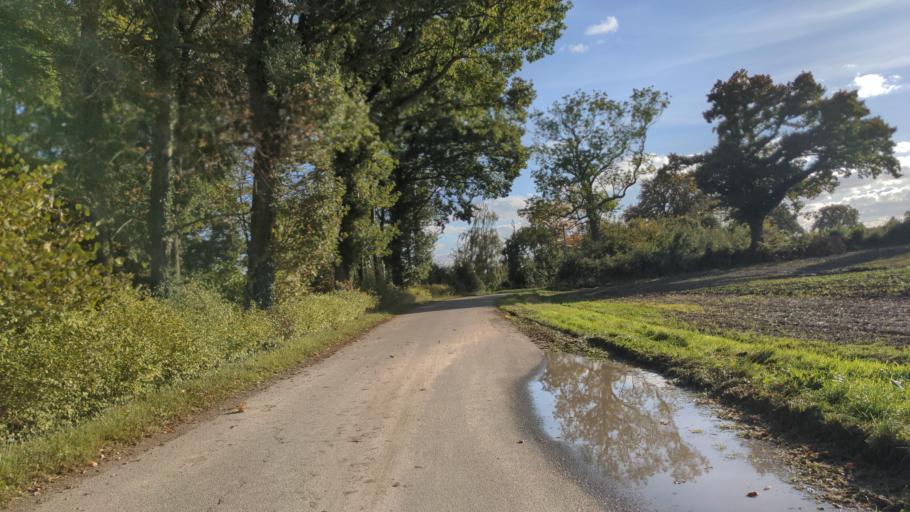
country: DE
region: Schleswig-Holstein
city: Manhagen
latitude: 54.1779
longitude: 10.9154
